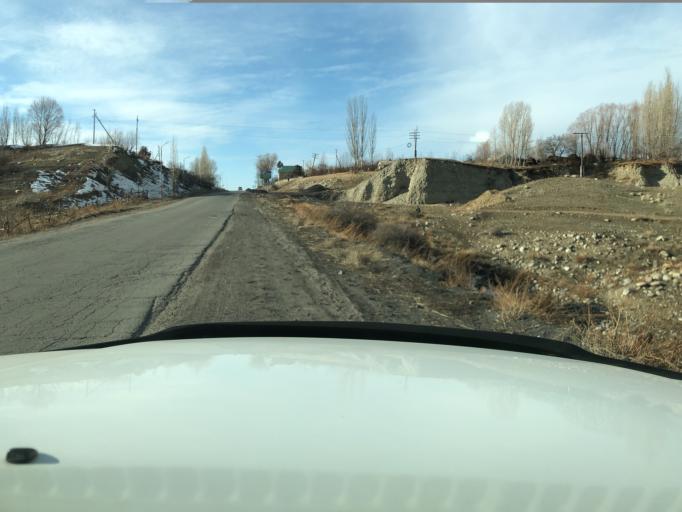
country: KG
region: Ysyk-Koel
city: Pokrovka
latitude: 42.3182
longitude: 77.9011
